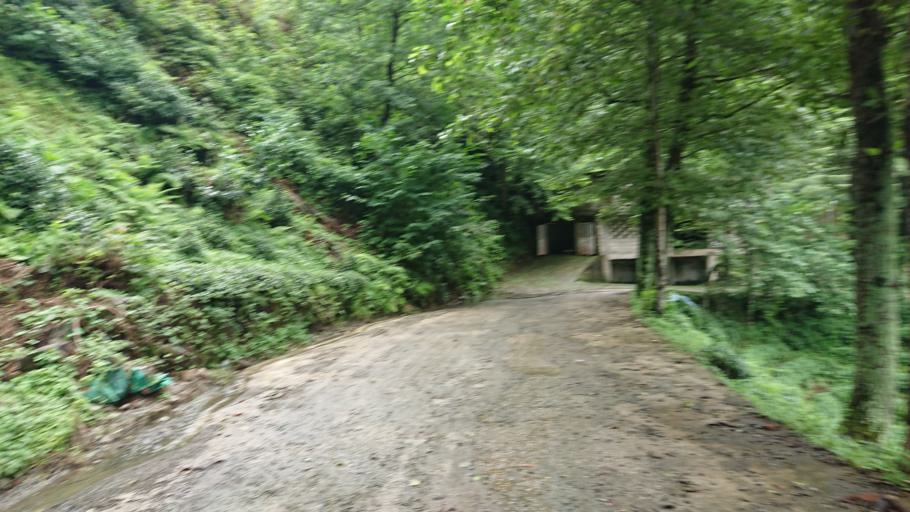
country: TR
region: Rize
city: Rize
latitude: 40.9770
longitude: 40.4852
